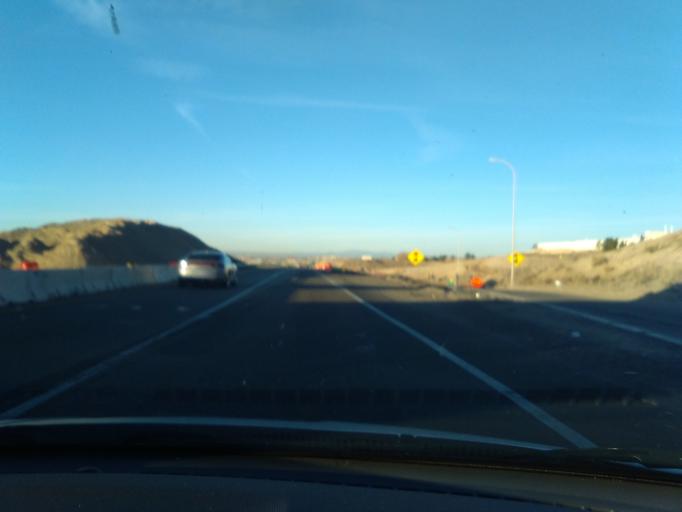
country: US
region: New Mexico
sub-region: Bernalillo County
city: South Valley
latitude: 35.0216
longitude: -106.6381
